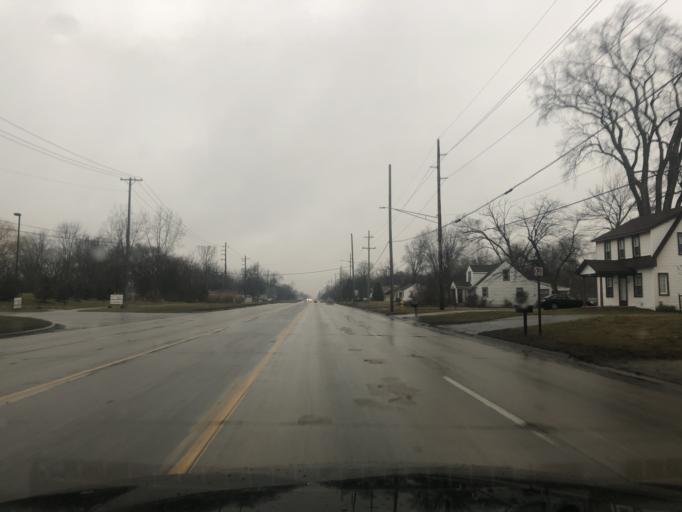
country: US
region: Michigan
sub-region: Wayne County
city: Inkster
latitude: 42.2681
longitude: -83.3154
